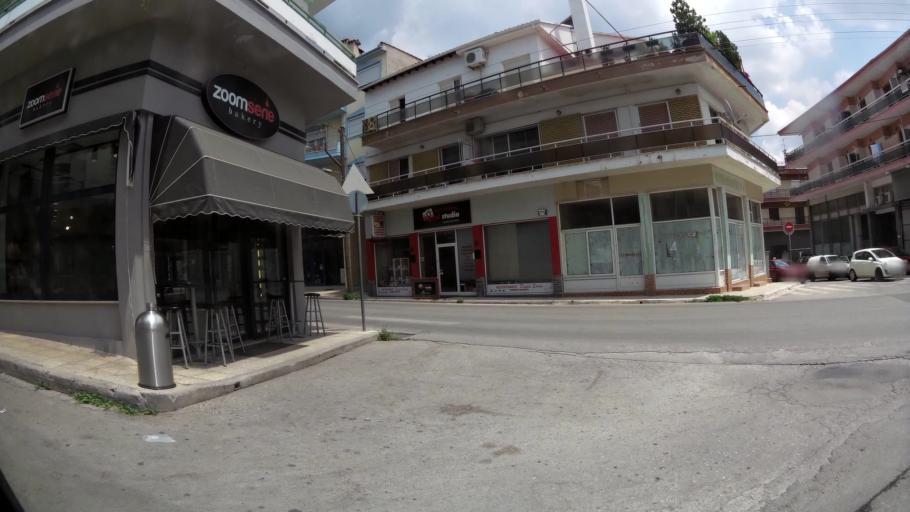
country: GR
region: West Macedonia
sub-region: Nomos Kozanis
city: Kozani
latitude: 40.2949
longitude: 21.7844
